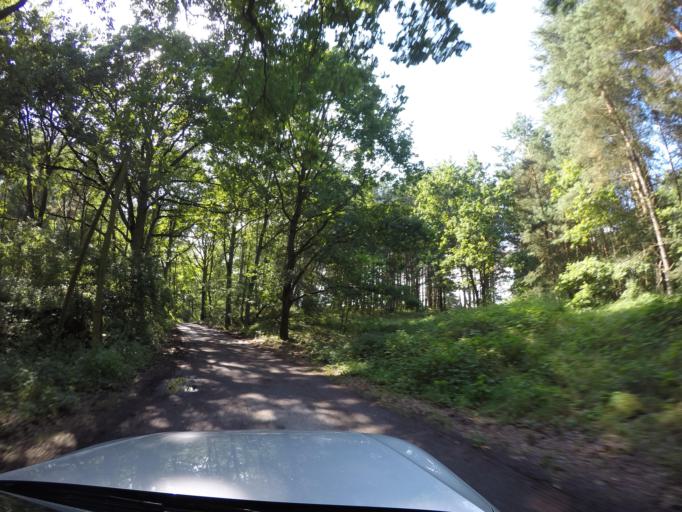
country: DE
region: Mecklenburg-Vorpommern
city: Wesenberg
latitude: 53.3665
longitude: 12.8913
